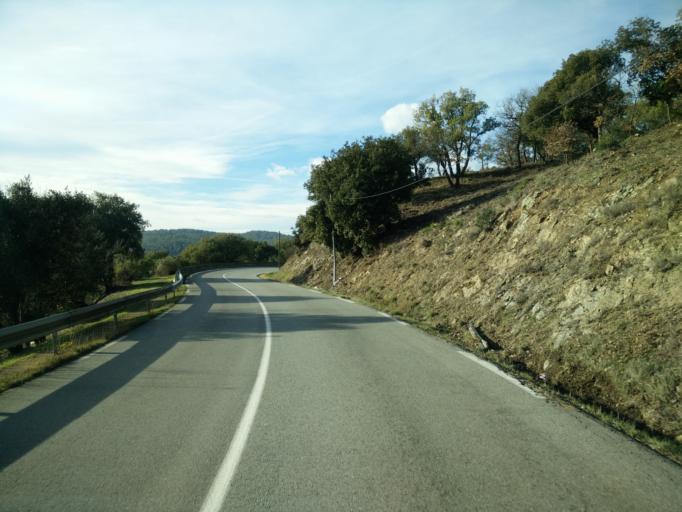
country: FR
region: Provence-Alpes-Cote d'Azur
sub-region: Departement du Var
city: Montauroux
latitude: 43.5867
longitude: 6.7938
